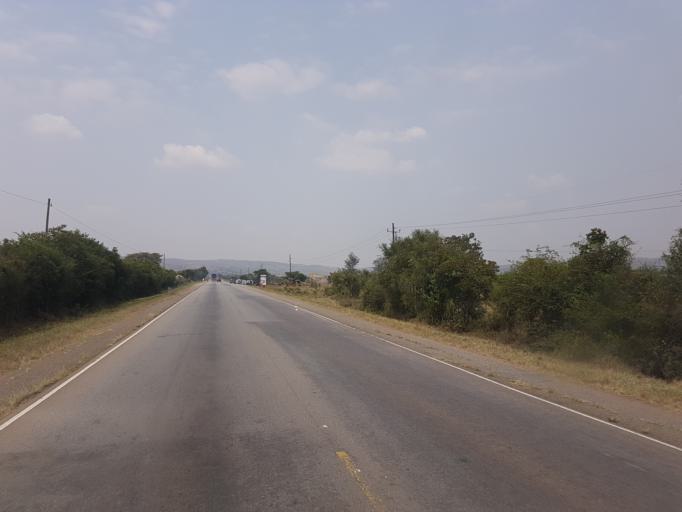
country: UG
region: Western Region
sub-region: Mbarara District
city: Mbarara
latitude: -0.5107
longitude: 30.8202
